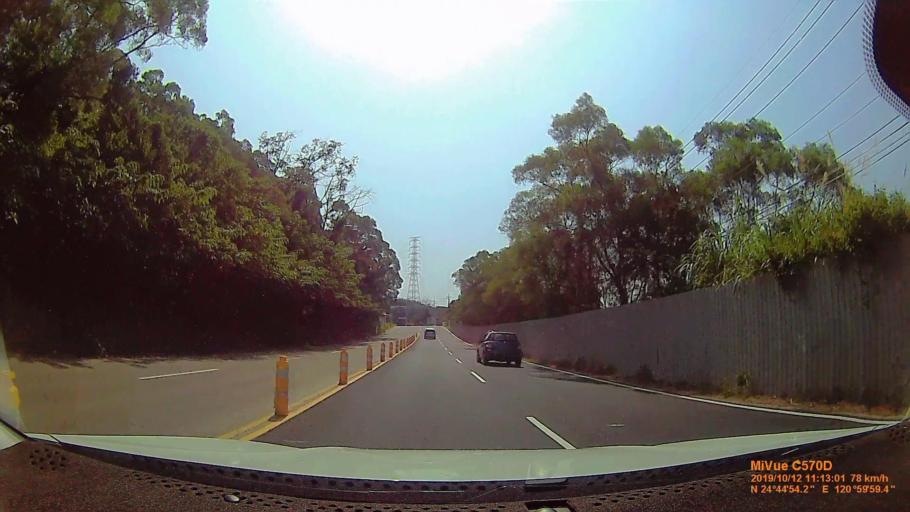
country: TW
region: Taiwan
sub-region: Hsinchu
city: Hsinchu
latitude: 24.7482
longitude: 120.9999
